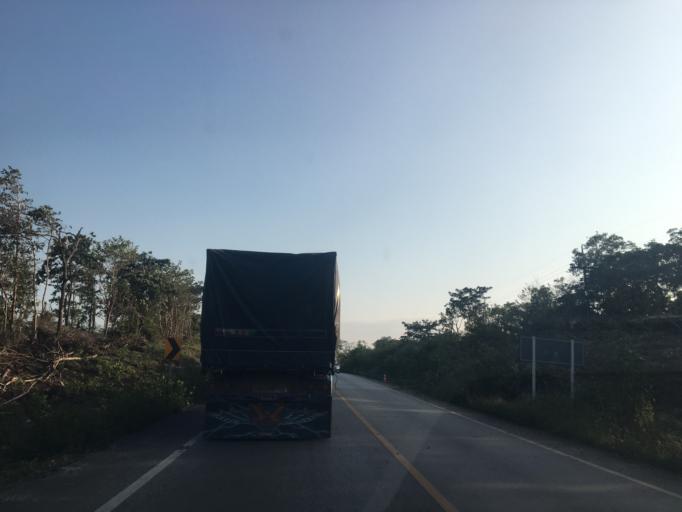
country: TH
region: Lampang
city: Ngao
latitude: 18.6611
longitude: 100.0175
